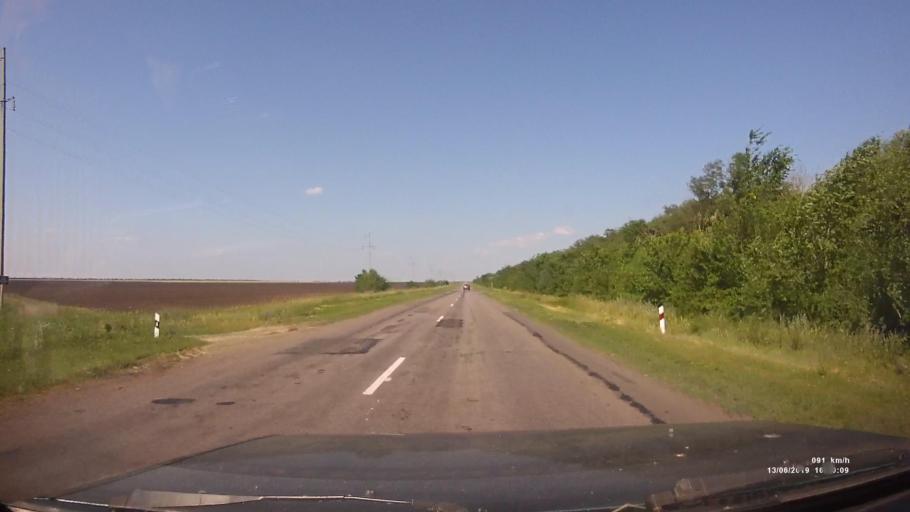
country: RU
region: Rostov
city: Kazanskaya
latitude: 49.8360
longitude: 41.2293
